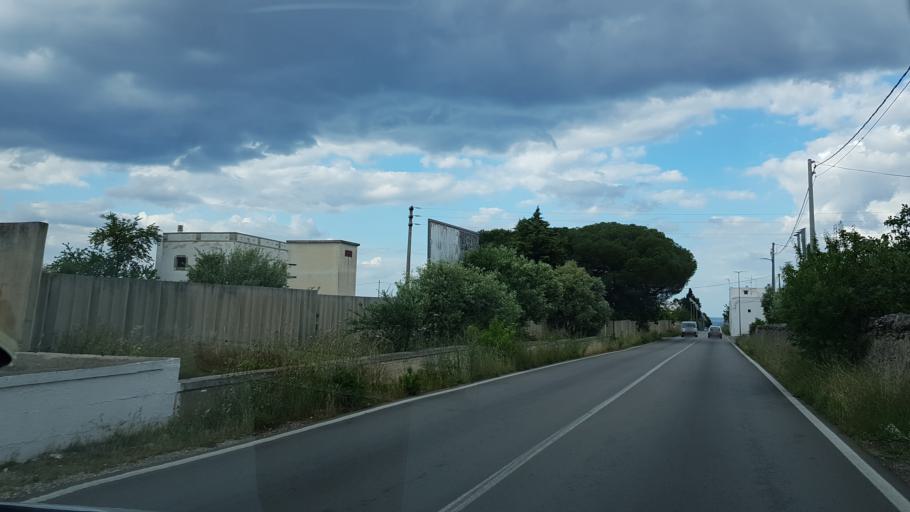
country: IT
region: Apulia
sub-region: Provincia di Brindisi
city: Fasano
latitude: 40.8460
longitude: 17.3813
